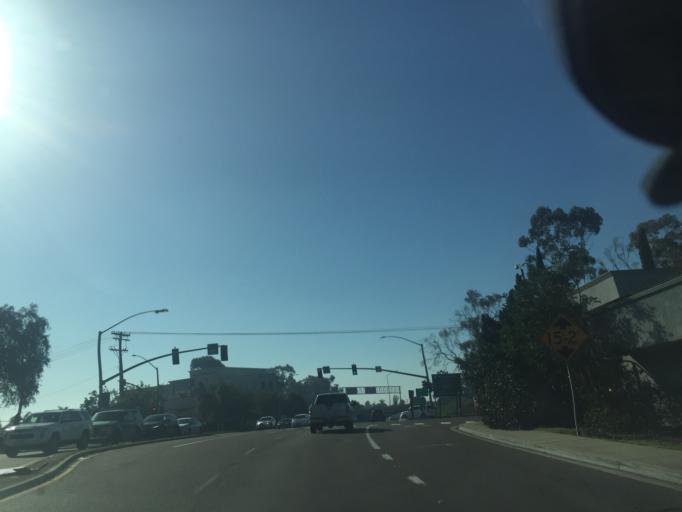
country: US
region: California
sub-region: San Diego County
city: San Diego
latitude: 32.7924
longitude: -117.1569
